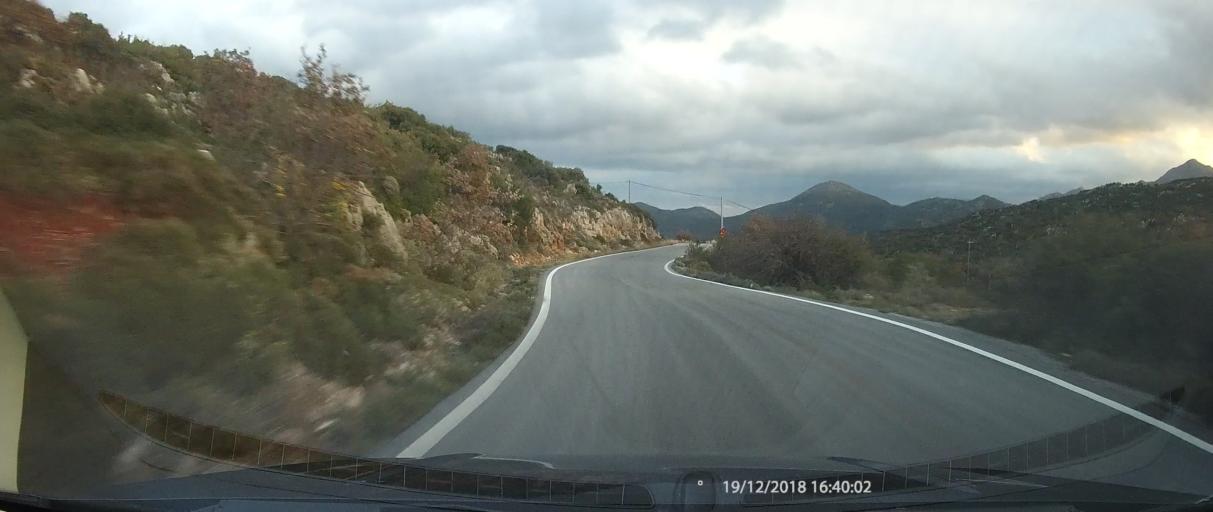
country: GR
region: Peloponnese
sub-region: Nomos Lakonias
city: Sykea
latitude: 36.9006
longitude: 22.9794
